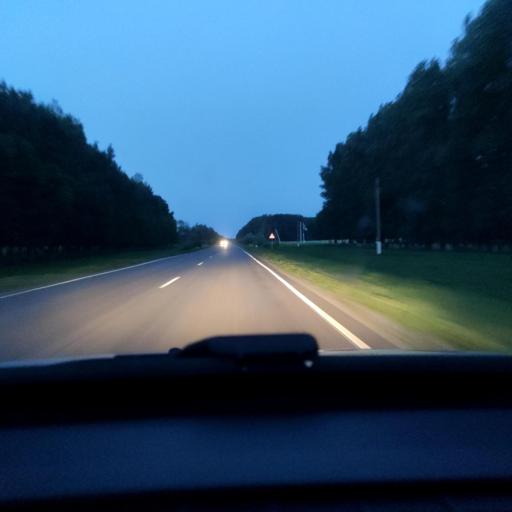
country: RU
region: Voronezj
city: Panino
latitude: 51.6631
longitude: 39.9786
